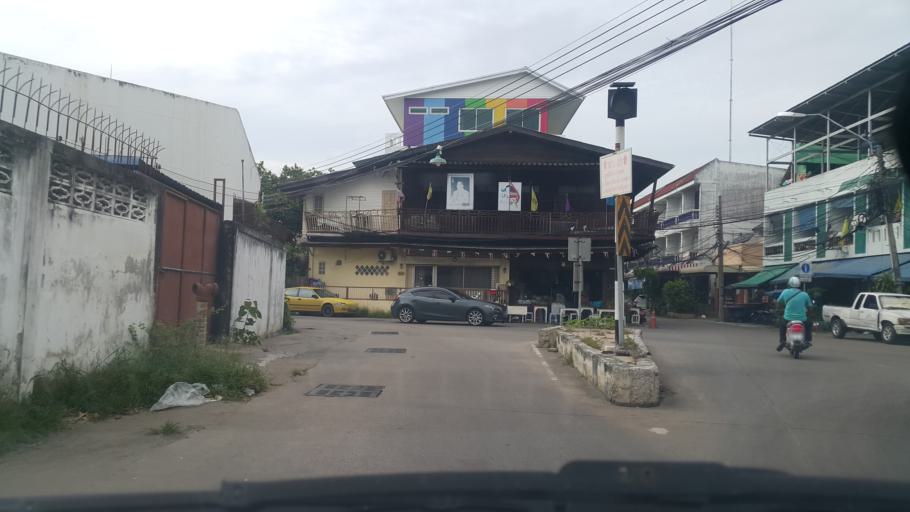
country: TH
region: Chon Buri
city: Phatthaya
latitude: 12.9713
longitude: 100.9087
